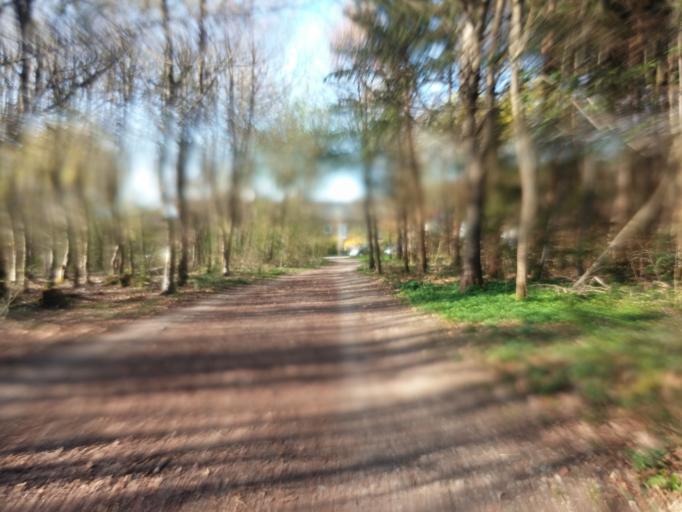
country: DE
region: Bavaria
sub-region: Upper Bavaria
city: Neubiberg
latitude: 48.1046
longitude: 11.6774
